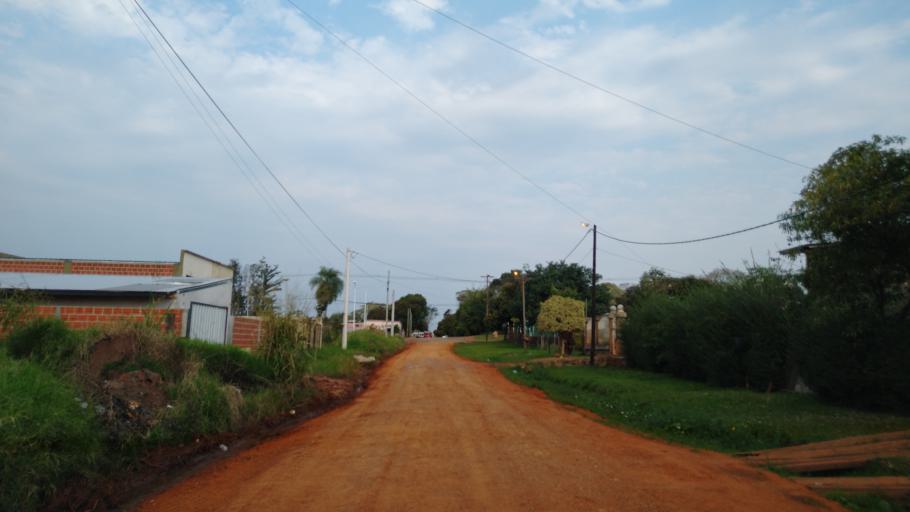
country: AR
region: Misiones
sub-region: Departamento de Capital
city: Posadas
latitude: -27.4256
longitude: -55.8781
